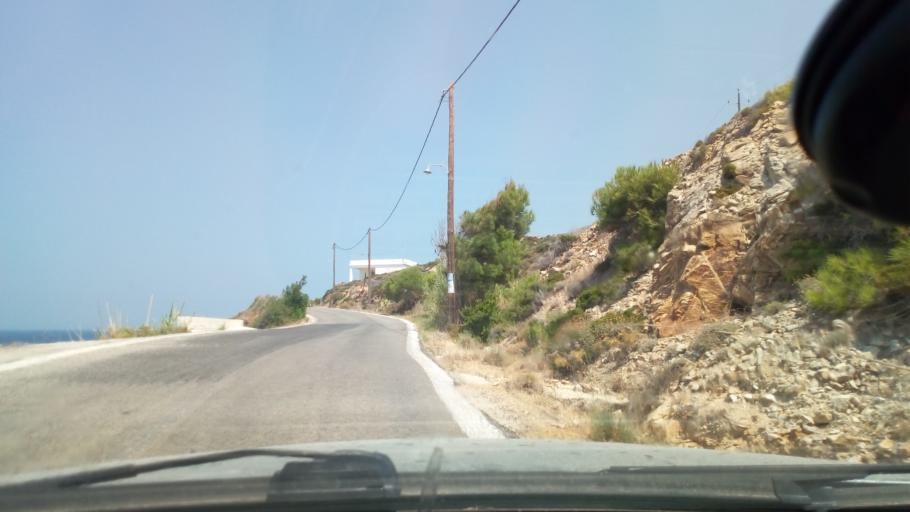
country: GR
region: North Aegean
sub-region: Nomos Samou
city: Agios Kirykos
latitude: 37.6317
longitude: 26.1125
